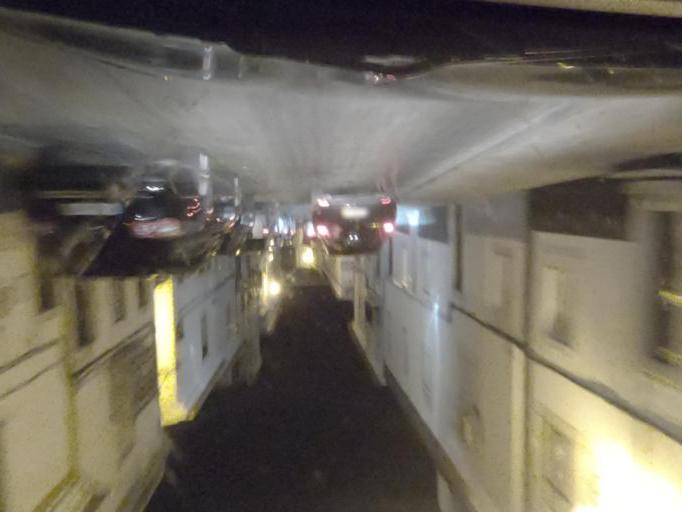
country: PT
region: Evora
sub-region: Estremoz
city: Estremoz
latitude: 38.8448
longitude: -7.5894
